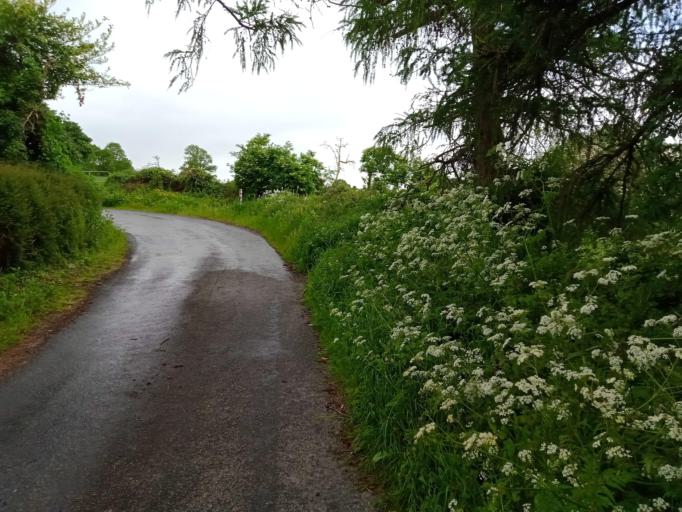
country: IE
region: Leinster
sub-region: Kilkenny
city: Thomastown
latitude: 52.5165
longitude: -7.1364
